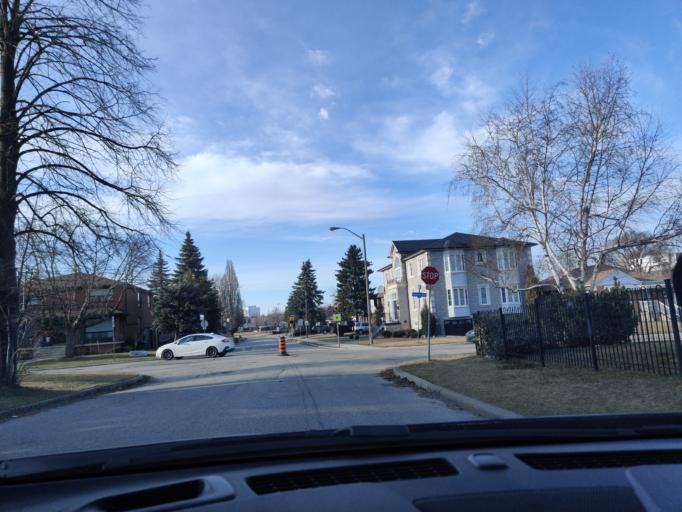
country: CA
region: Ontario
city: Toronto
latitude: 43.7047
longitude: -79.4448
